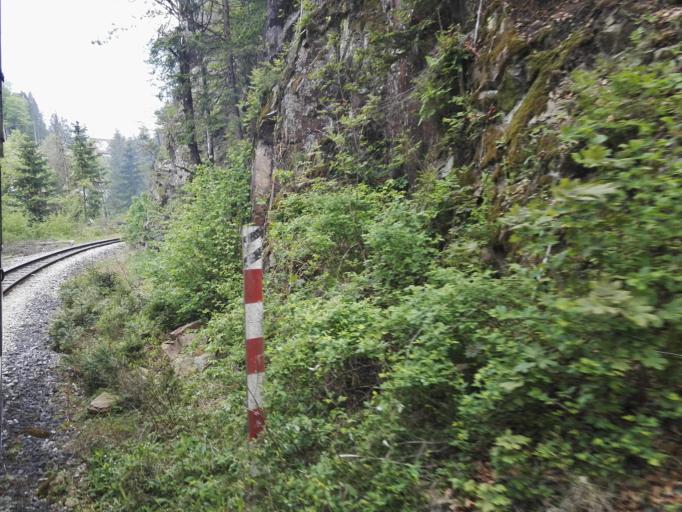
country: AT
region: Styria
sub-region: Politischer Bezirk Weiz
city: Birkfeld
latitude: 47.3435
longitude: 15.6991
